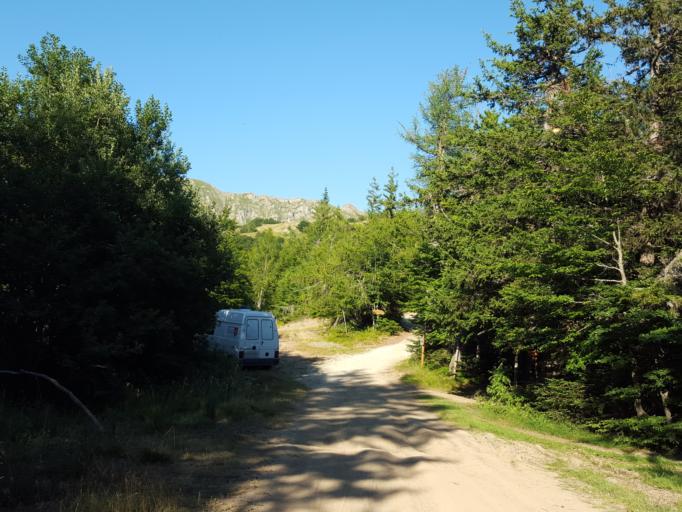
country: IT
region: Tuscany
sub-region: Provincia di Pistoia
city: Abetone
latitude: 44.1566
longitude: 10.6870
